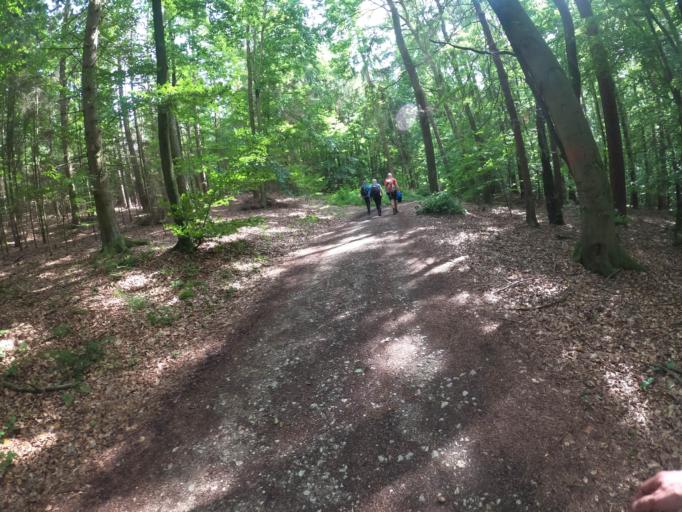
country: DE
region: Bavaria
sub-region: Upper Franconia
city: Litzendorf
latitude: 49.9080
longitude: 11.0331
